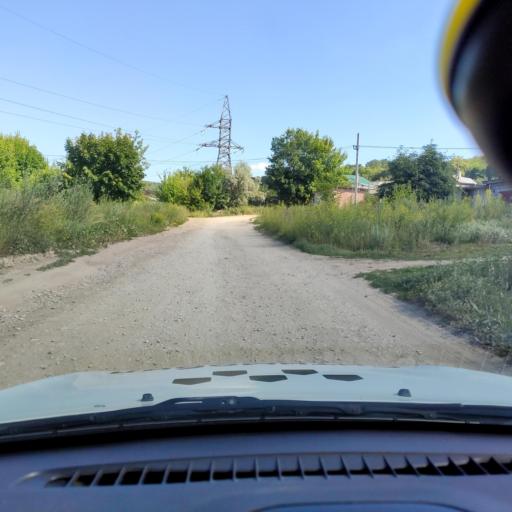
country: RU
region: Samara
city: Zhigulevsk
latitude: 53.4003
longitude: 49.5228
